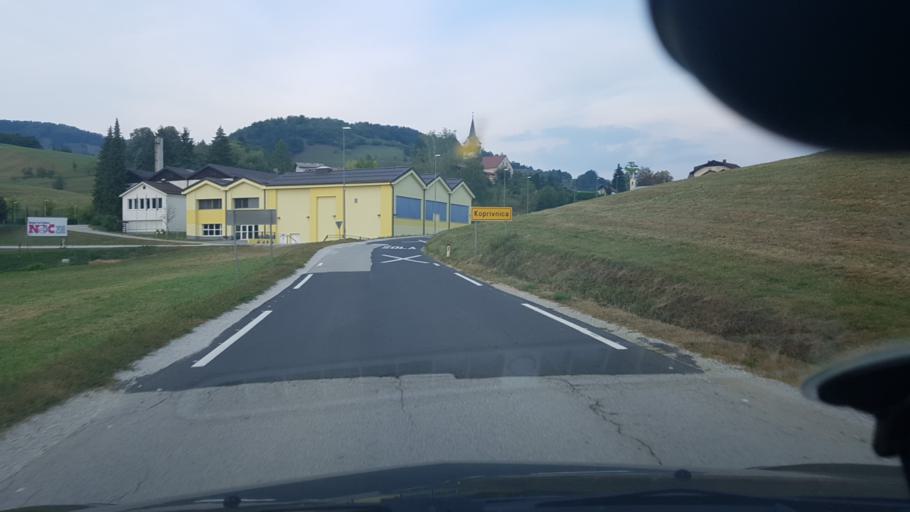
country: SI
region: Kozje
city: Kozje
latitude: 46.0344
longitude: 15.5372
